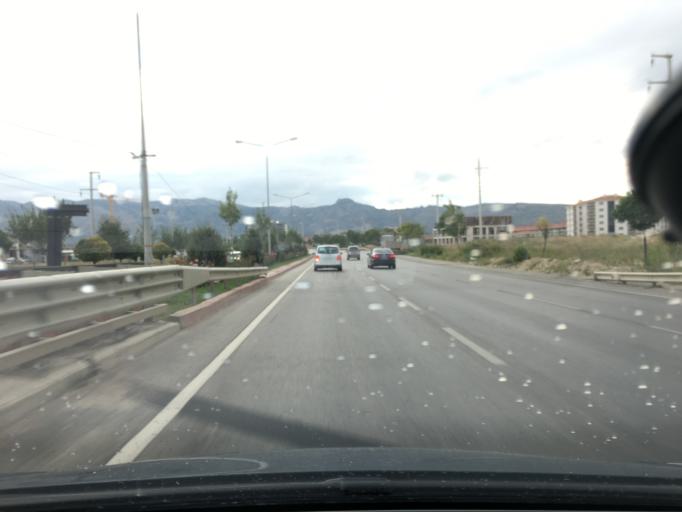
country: TR
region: Afyonkarahisar
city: Afyonkarahisar
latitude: 38.7853
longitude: 30.5024
